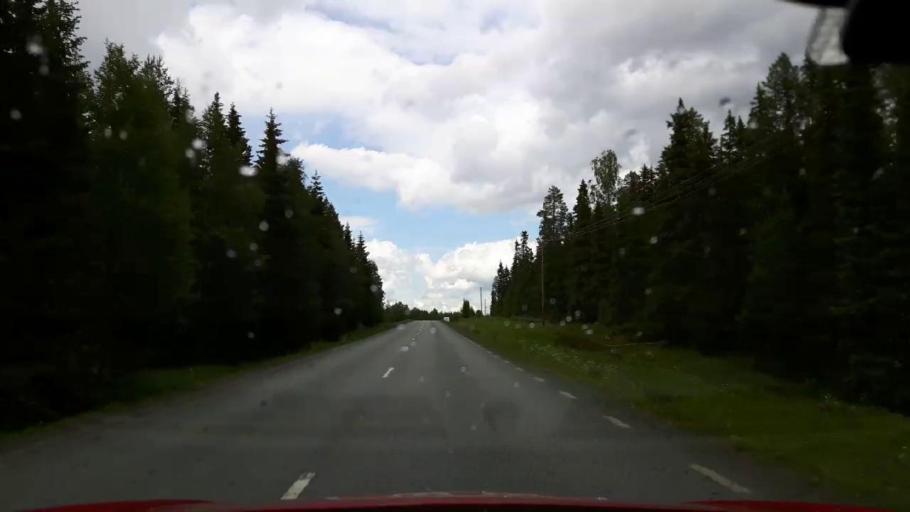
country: SE
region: Jaemtland
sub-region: Krokoms Kommun
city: Krokom
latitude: 63.5345
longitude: 14.2508
